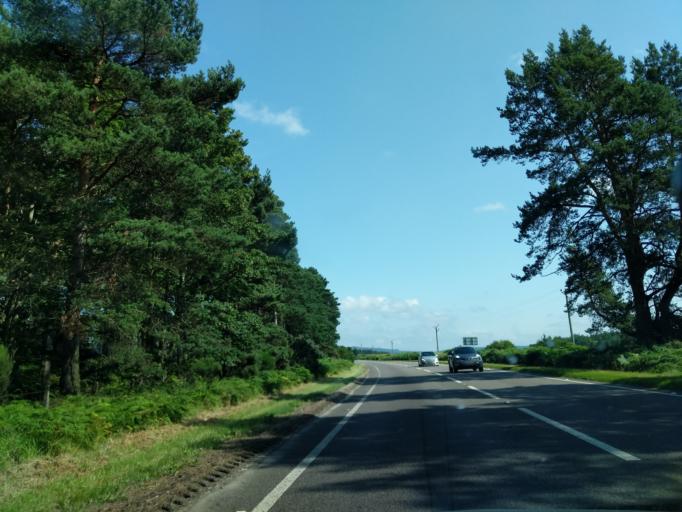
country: GB
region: Scotland
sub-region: Moray
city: Lhanbryd
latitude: 57.6328
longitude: -3.1847
